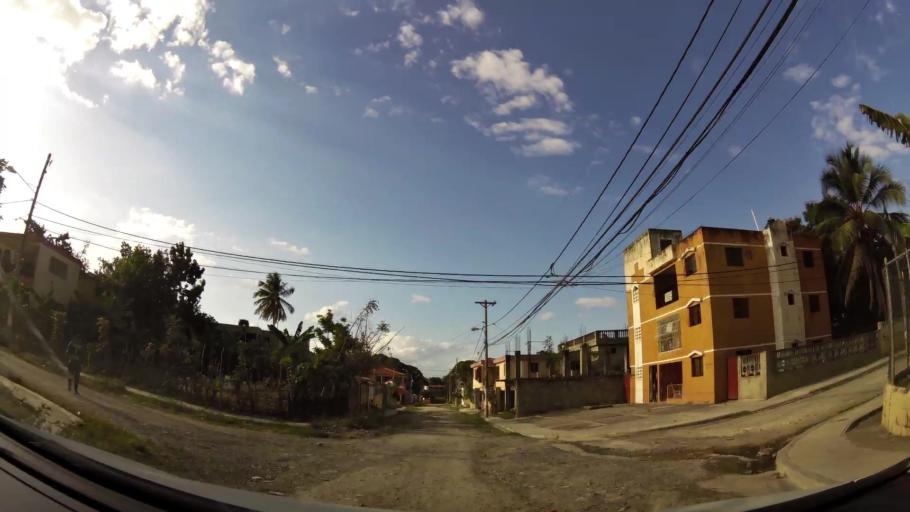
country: DO
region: Nacional
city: Ensanche Luperon
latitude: 18.5589
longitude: -69.8944
